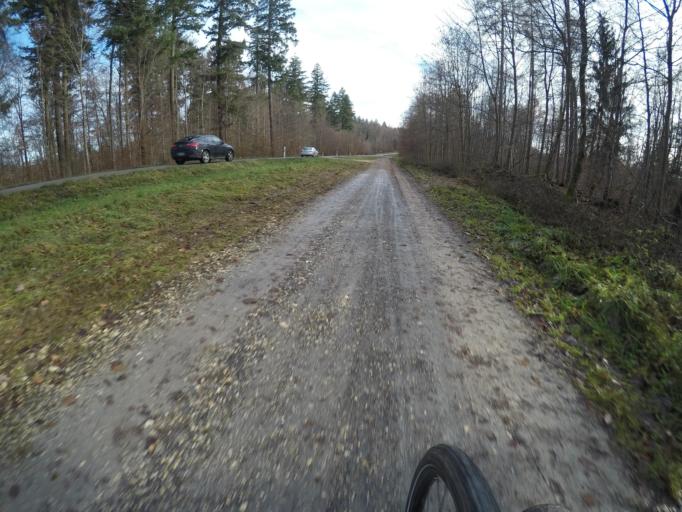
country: DE
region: Baden-Wuerttemberg
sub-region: Regierungsbezirk Stuttgart
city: Winterbach
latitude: 48.7664
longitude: 9.4812
